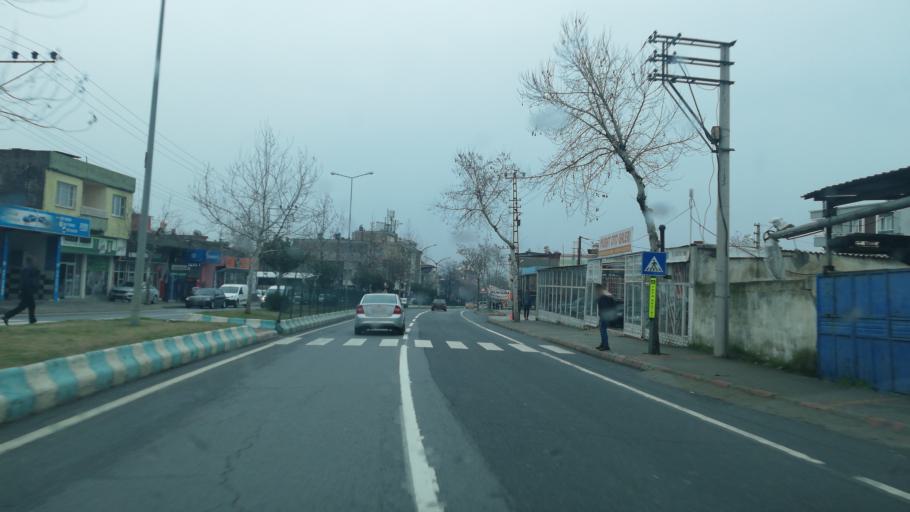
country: TR
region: Kahramanmaras
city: Kahramanmaras
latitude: 37.5700
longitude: 36.9454
